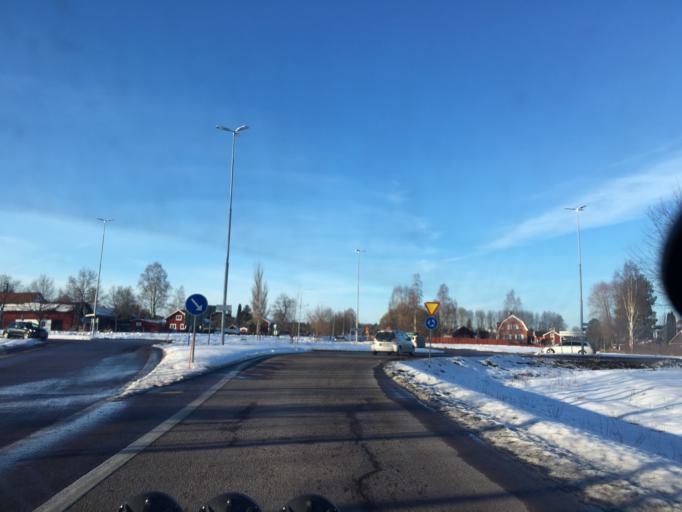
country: SE
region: Dalarna
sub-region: Borlange Kommun
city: Borlaenge
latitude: 60.4691
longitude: 15.3942
